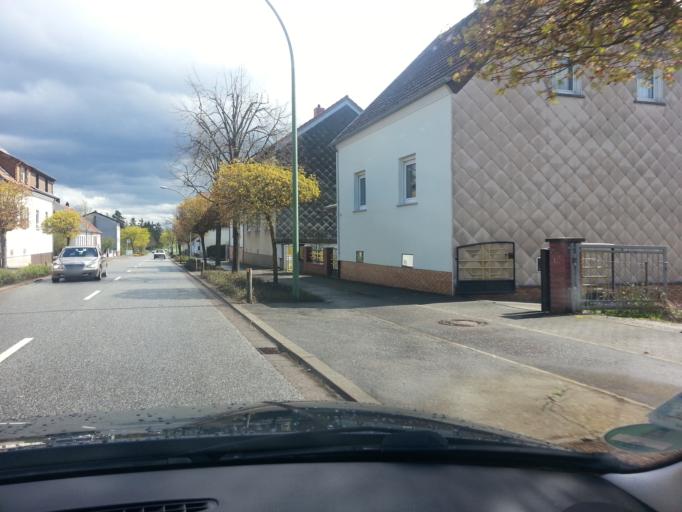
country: DE
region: Saarland
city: Bexbach
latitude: 49.3150
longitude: 7.2501
